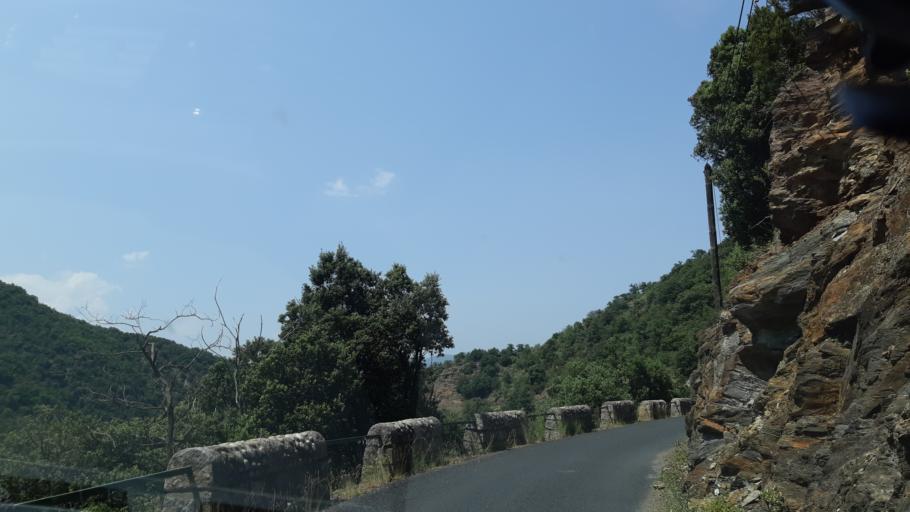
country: FR
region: Languedoc-Roussillon
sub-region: Departement des Pyrenees-Orientales
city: Vinca
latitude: 42.6058
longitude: 2.5138
